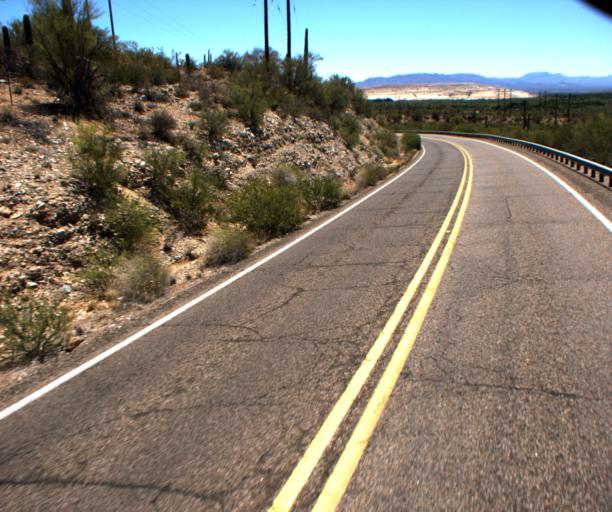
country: US
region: Arizona
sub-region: Pinal County
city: Kearny
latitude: 33.0172
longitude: -110.8453
